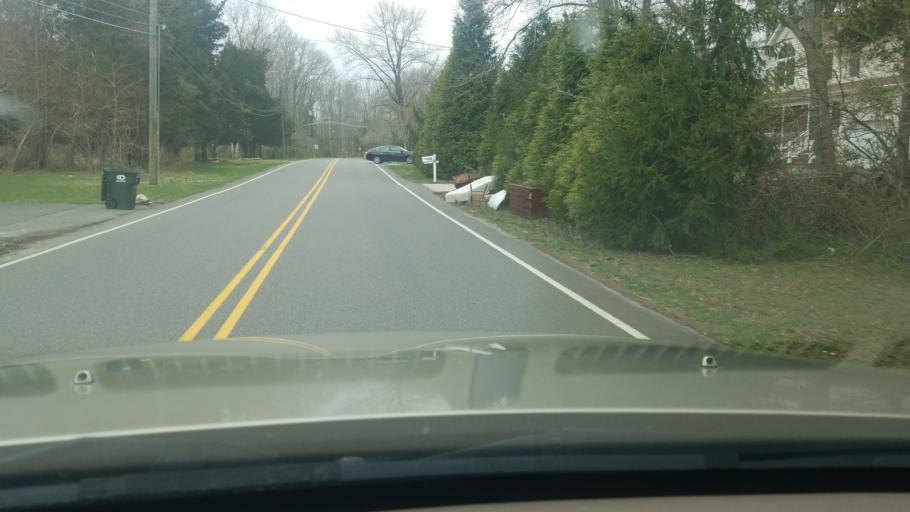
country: US
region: New Jersey
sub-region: Ocean County
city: Lakewood
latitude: 40.1161
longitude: -74.2064
